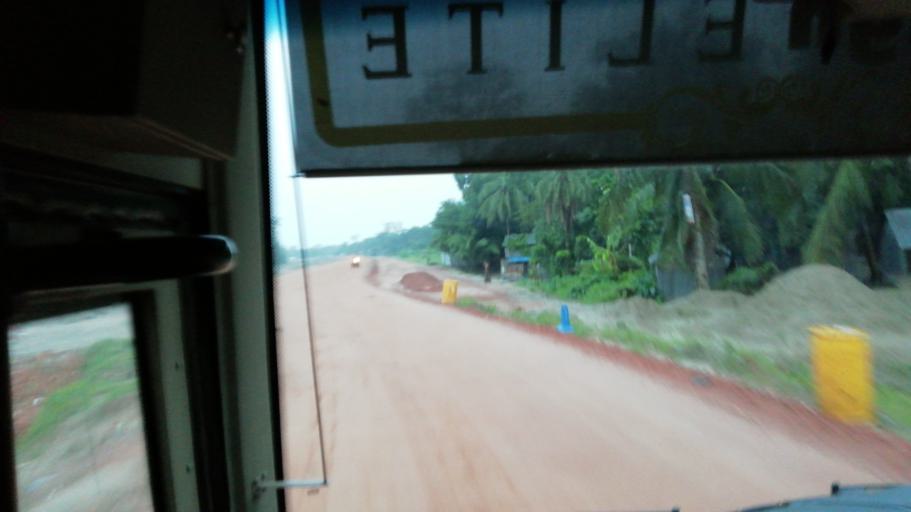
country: BD
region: Dhaka
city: Char Bhadrasan
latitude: 23.3999
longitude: 90.1306
